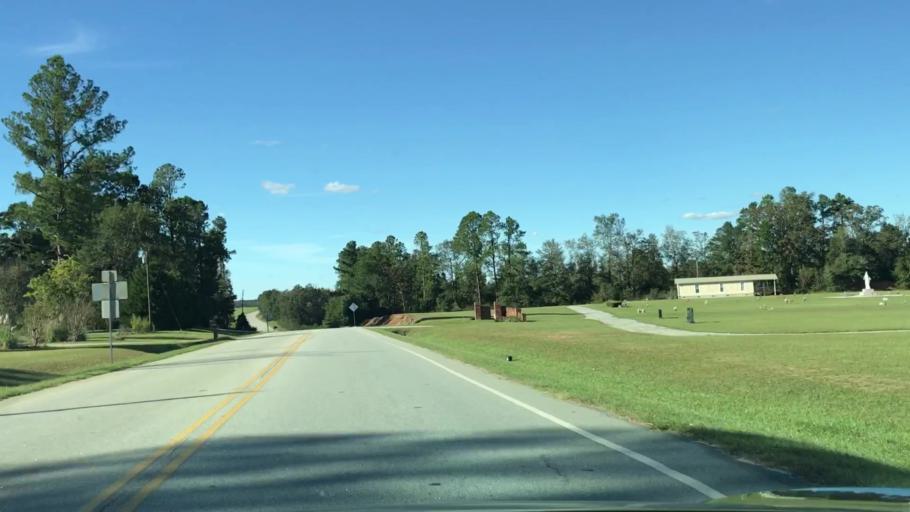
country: US
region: Georgia
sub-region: Jefferson County
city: Louisville
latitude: 33.0696
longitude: -82.4071
